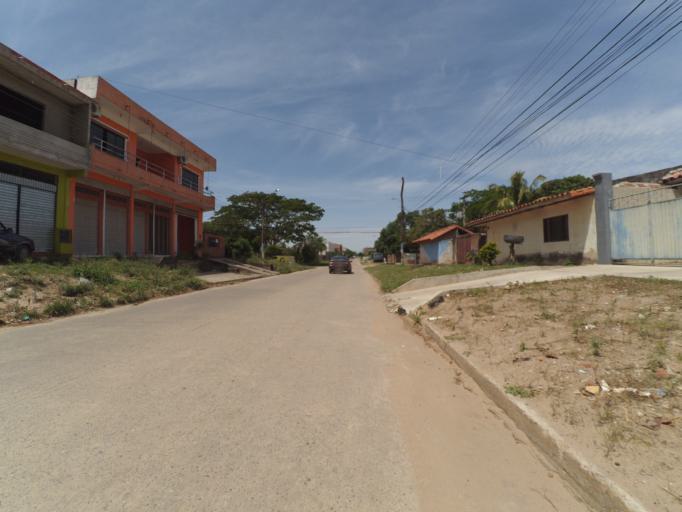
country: BO
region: Santa Cruz
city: Santa Cruz de la Sierra
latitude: -17.8277
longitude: -63.2312
